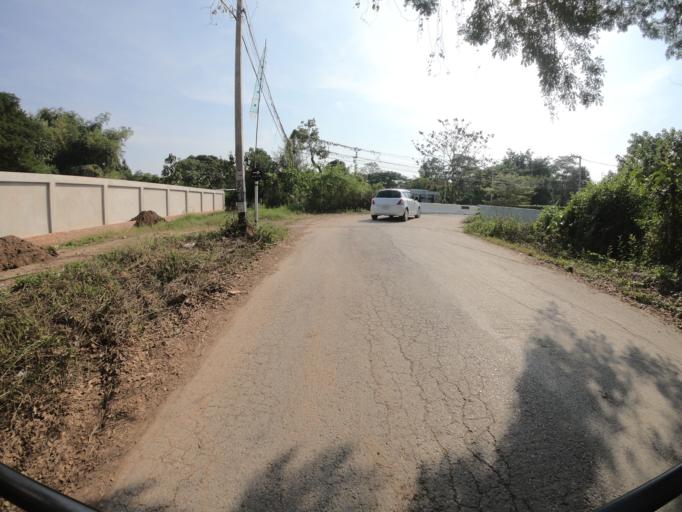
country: TH
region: Chiang Mai
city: San Sai
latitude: 18.8423
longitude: 99.0075
